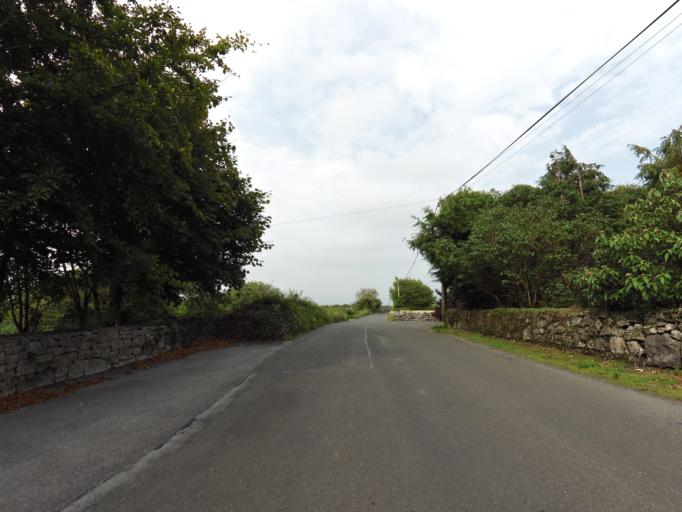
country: IE
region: Connaught
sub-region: County Galway
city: Gaillimh
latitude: 53.3040
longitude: -9.0643
